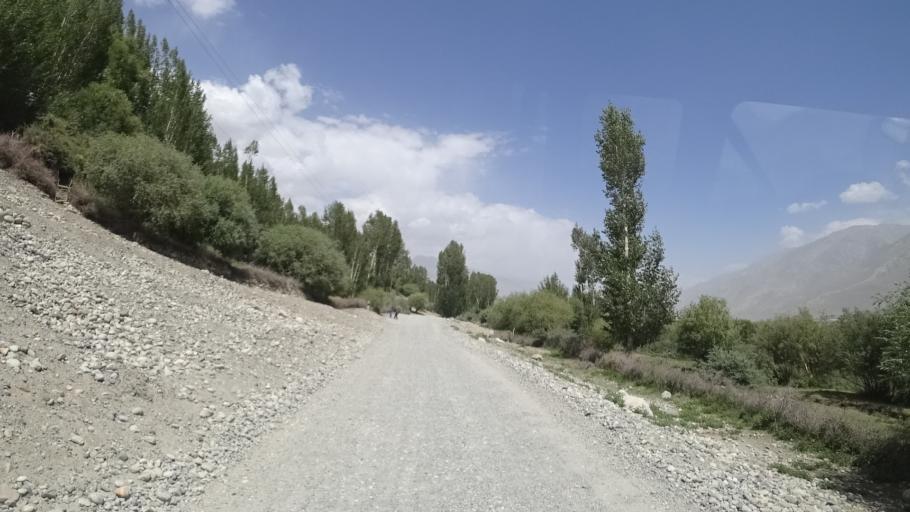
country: AF
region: Badakhshan
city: Khandud
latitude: 36.9386
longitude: 72.2205
